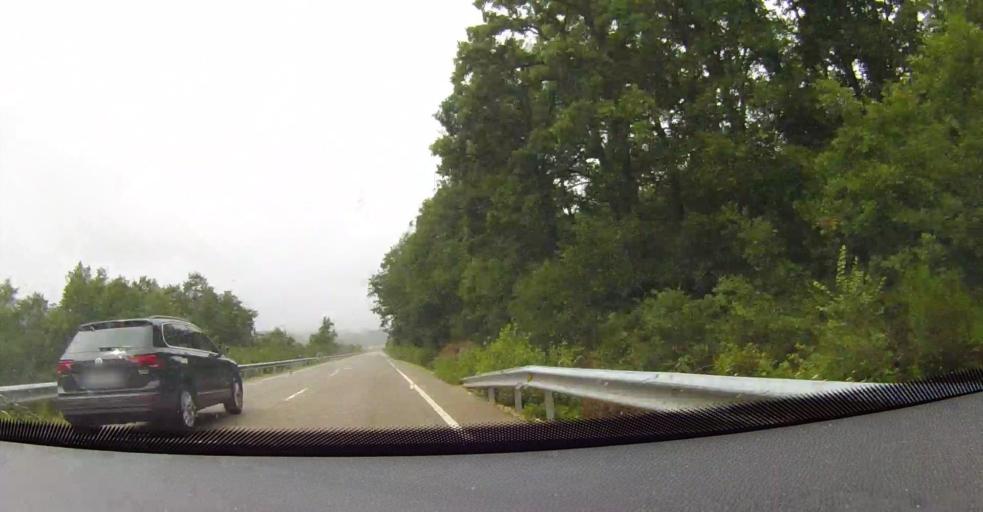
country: ES
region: Castille and Leon
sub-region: Provincia de Leon
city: Sabero
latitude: 42.8388
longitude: -5.2332
